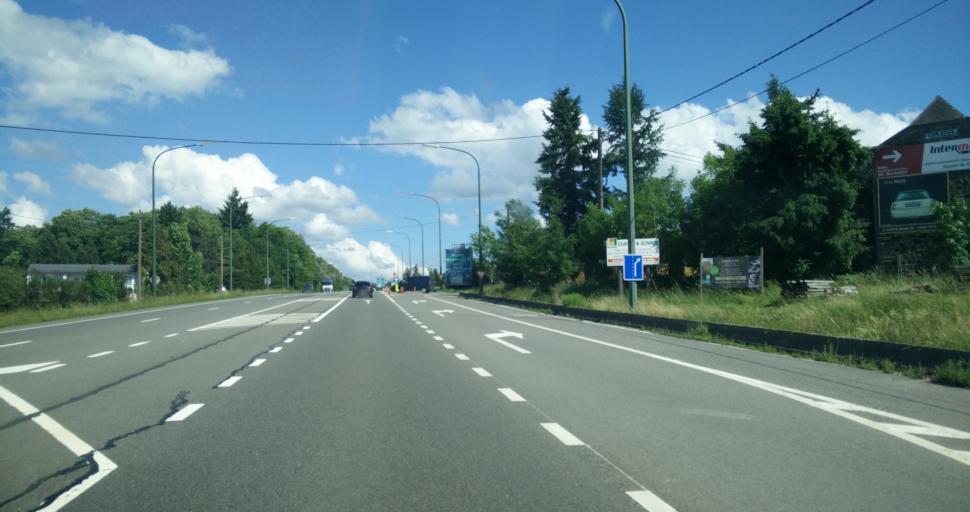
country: BE
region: Wallonia
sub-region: Province du Luxembourg
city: Marche-en-Famenne
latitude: 50.2320
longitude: 5.3182
